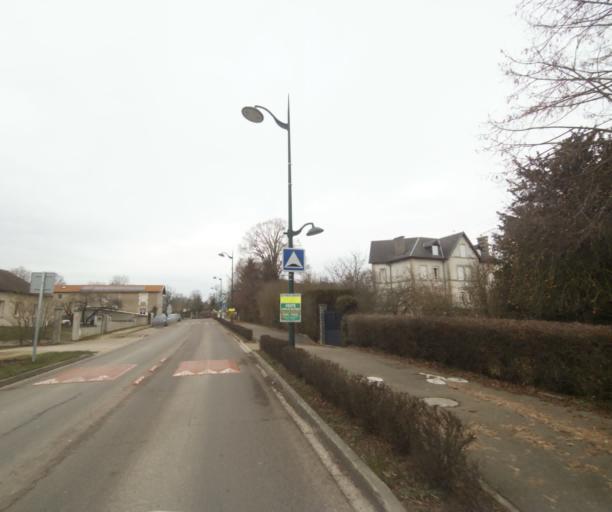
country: FR
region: Champagne-Ardenne
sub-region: Departement de la Haute-Marne
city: Villiers-en-Lieu
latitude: 48.6639
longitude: 4.9060
